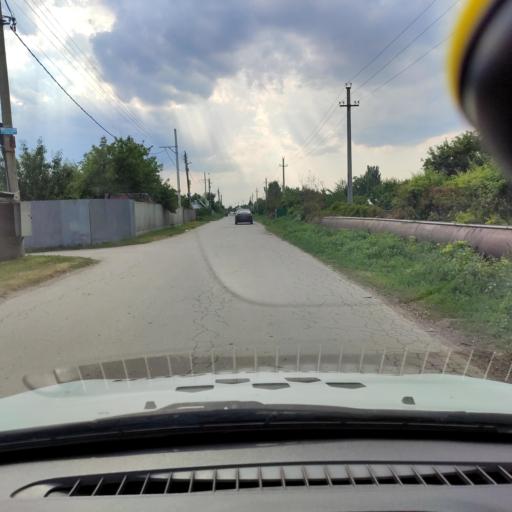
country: RU
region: Samara
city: Podstepki
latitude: 53.5075
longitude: 49.1419
